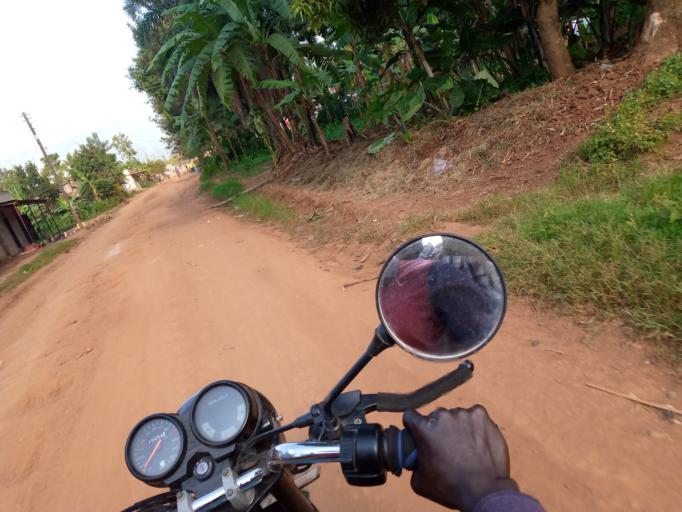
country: UG
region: Eastern Region
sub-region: Mbale District
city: Mbale
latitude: 1.0537
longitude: 34.1661
